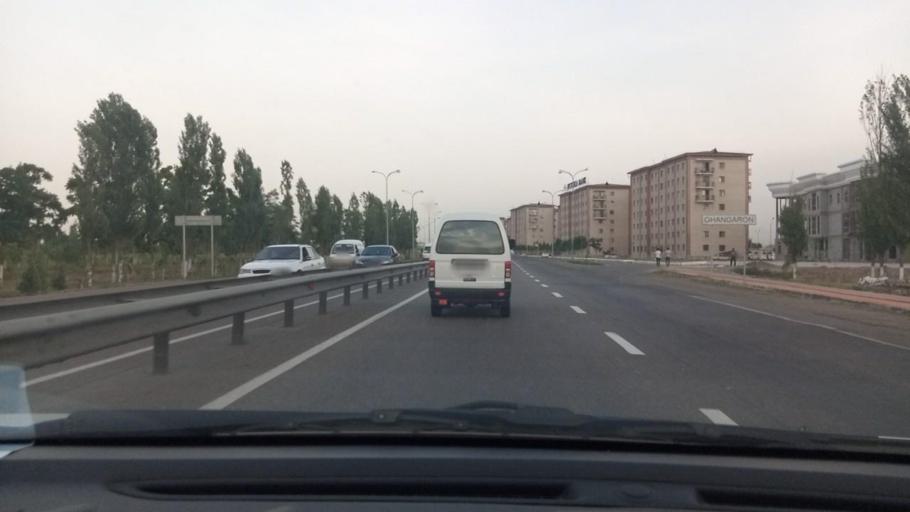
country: UZ
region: Toshkent
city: Ohangaron
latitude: 40.9157
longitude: 69.6064
